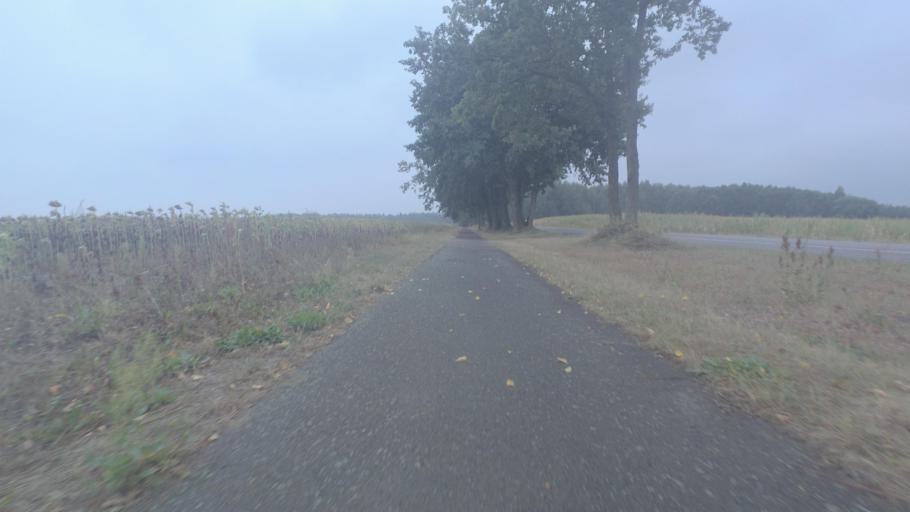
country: DE
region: Brandenburg
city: Heiligengrabe
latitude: 53.1372
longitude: 12.3699
